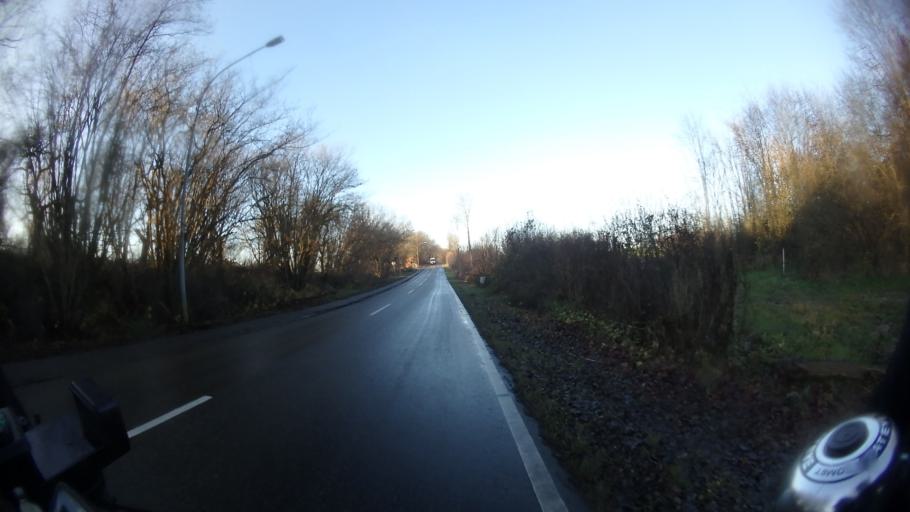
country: DE
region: Schleswig-Holstein
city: Travemuende
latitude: 53.9783
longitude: 10.8653
